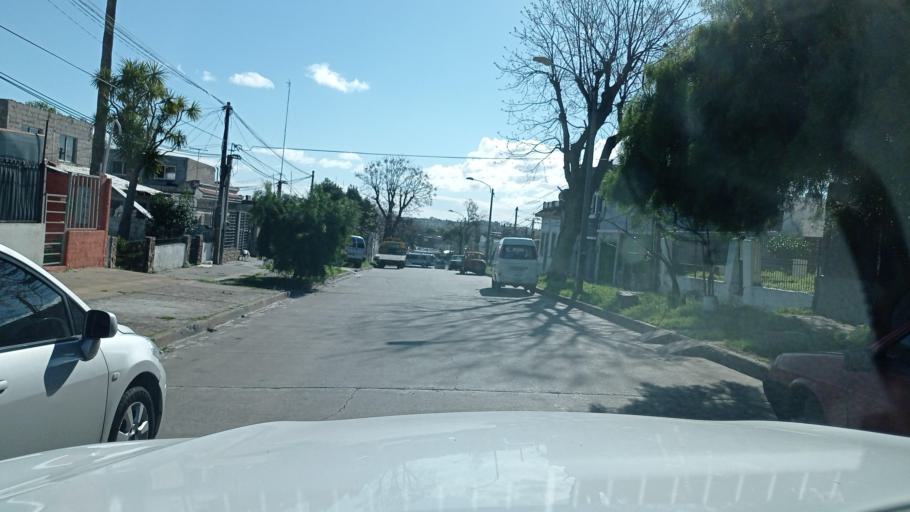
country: UY
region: Montevideo
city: Montevideo
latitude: -34.8512
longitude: -56.1776
